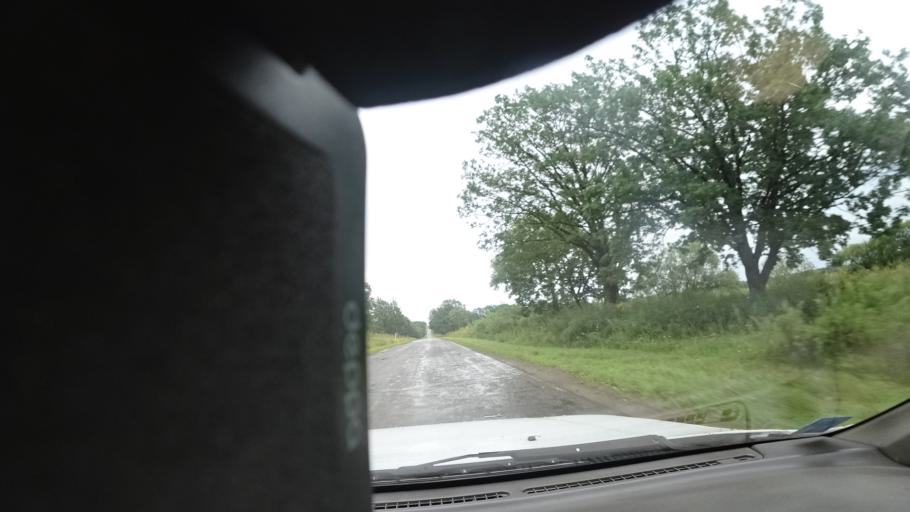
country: RU
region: Primorskiy
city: Lazo
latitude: 45.8701
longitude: 133.6958
